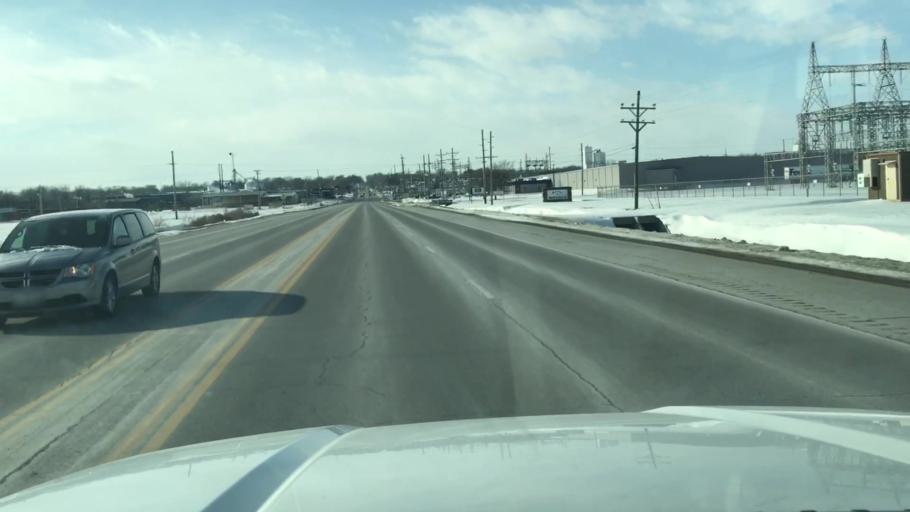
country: US
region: Missouri
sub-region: Nodaway County
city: Maryville
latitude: 40.3451
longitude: -94.8424
